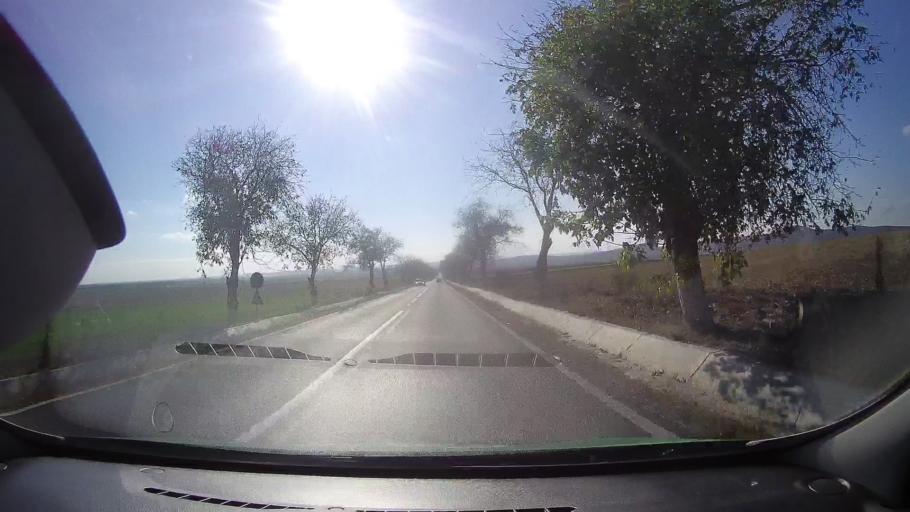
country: RO
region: Tulcea
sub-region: Comuna Ceamurlia de Jos
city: Ceamurlia de Jos
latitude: 44.8048
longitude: 28.6908
